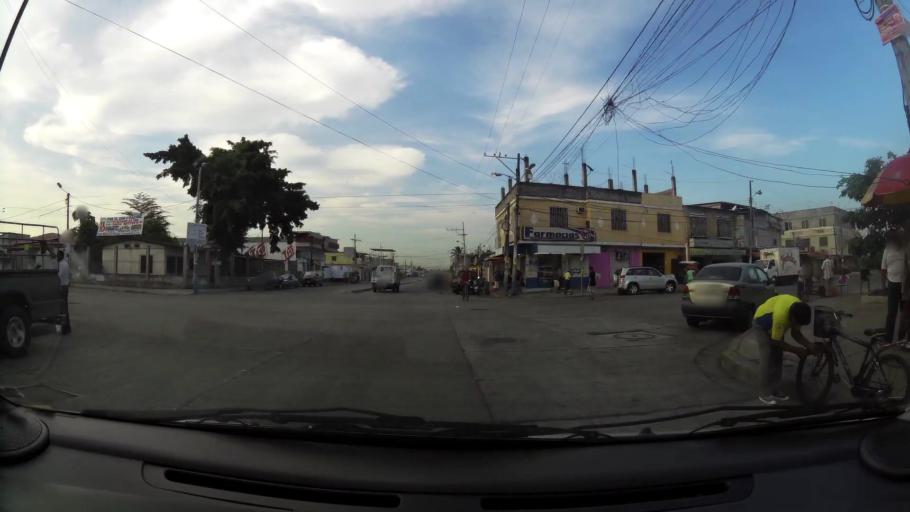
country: EC
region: Guayas
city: Eloy Alfaro
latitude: -2.0914
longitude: -79.9036
